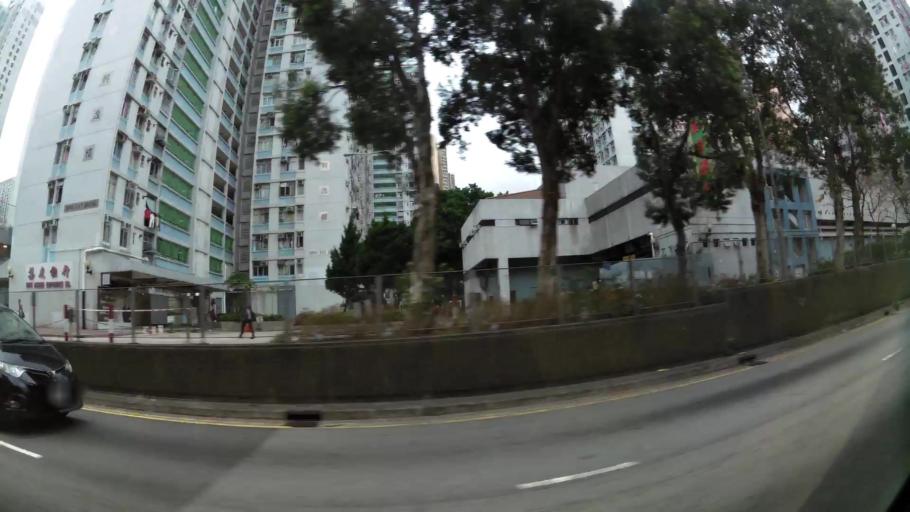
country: HK
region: Tsuen Wan
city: Tsuen Wan
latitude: 22.3663
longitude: 114.1333
